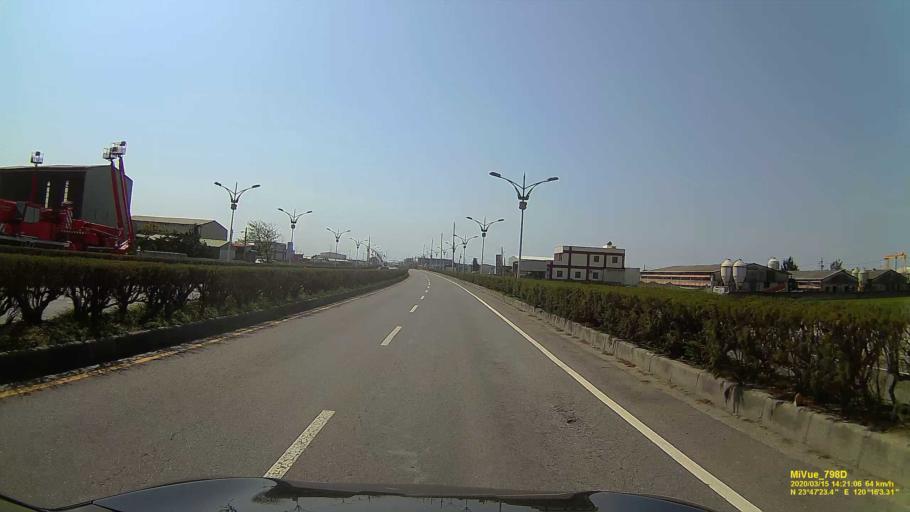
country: TW
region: Taiwan
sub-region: Yunlin
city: Douliu
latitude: 23.7899
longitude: 120.2673
